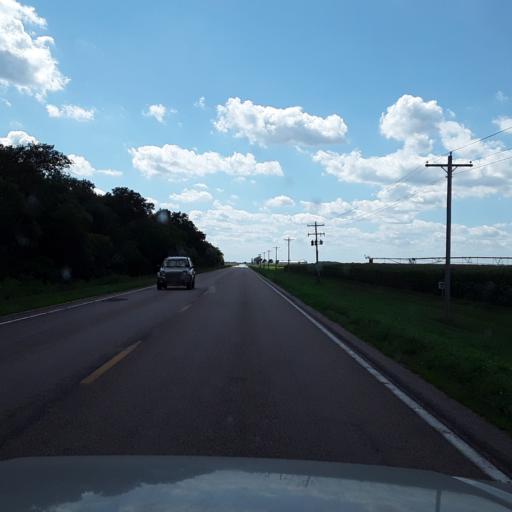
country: US
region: Nebraska
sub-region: Merrick County
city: Central City
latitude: 41.1910
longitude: -98.0236
